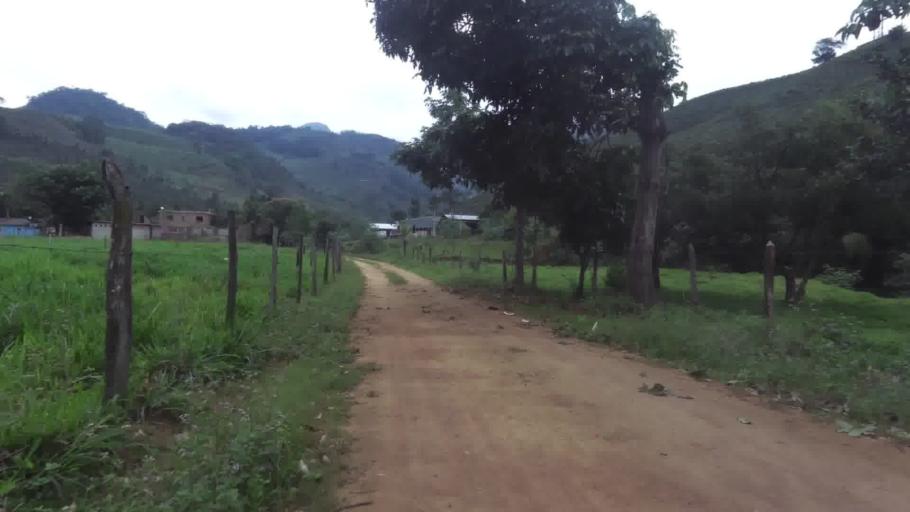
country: BR
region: Espirito Santo
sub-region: Iconha
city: Iconha
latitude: -20.7631
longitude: -40.8363
